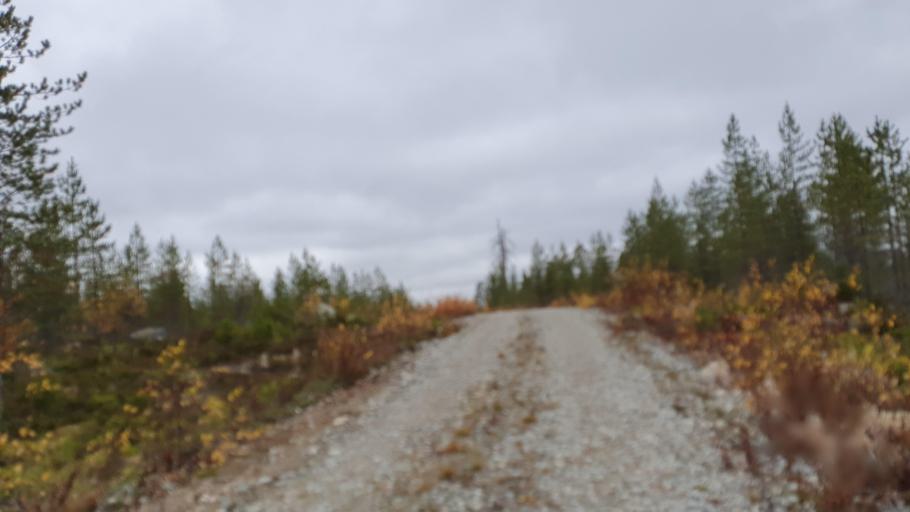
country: FI
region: Kainuu
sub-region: Kehys-Kainuu
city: Kuhmo
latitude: 64.4506
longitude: 29.5957
